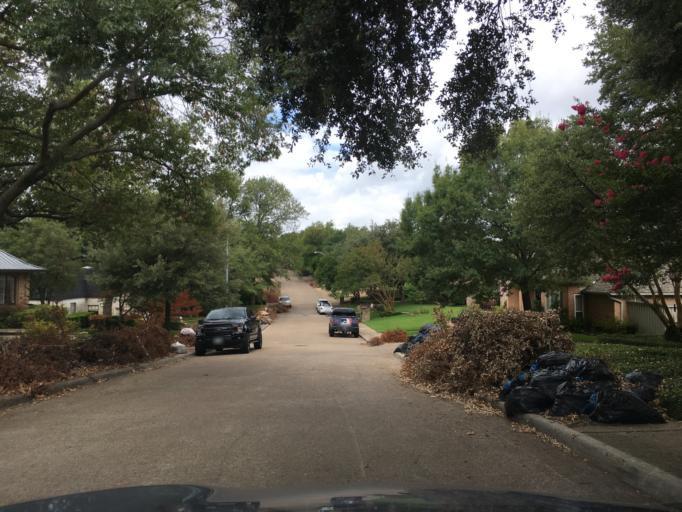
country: US
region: Texas
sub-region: Dallas County
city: Richardson
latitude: 32.8932
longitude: -96.7435
